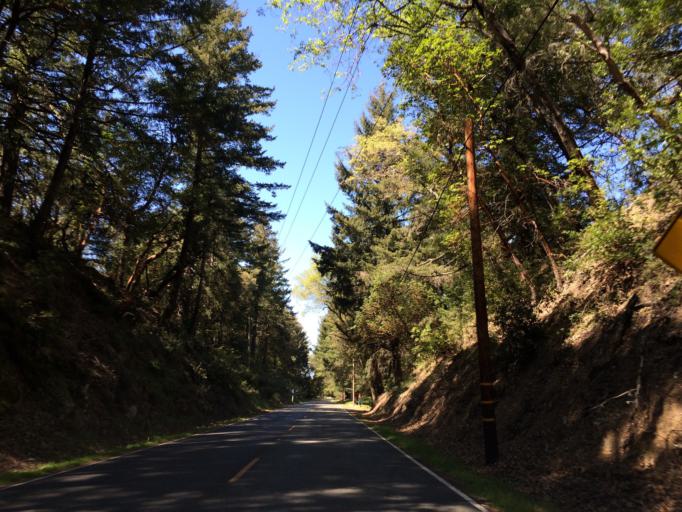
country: US
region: California
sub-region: Santa Clara County
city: Saratoga
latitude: 37.2423
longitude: -122.1072
